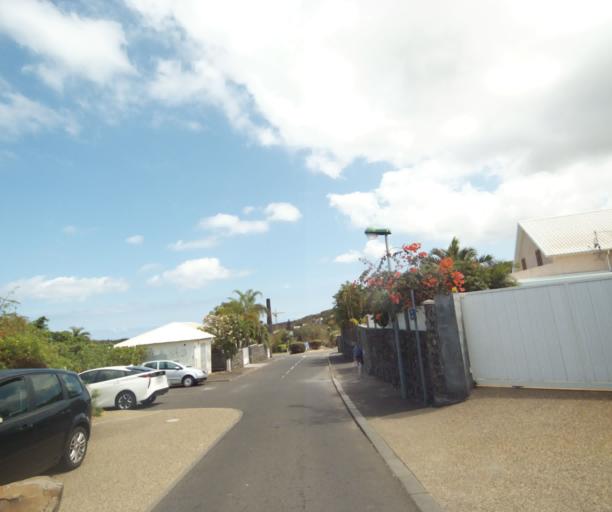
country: RE
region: Reunion
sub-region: Reunion
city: Trois-Bassins
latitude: -21.0848
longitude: 55.2380
